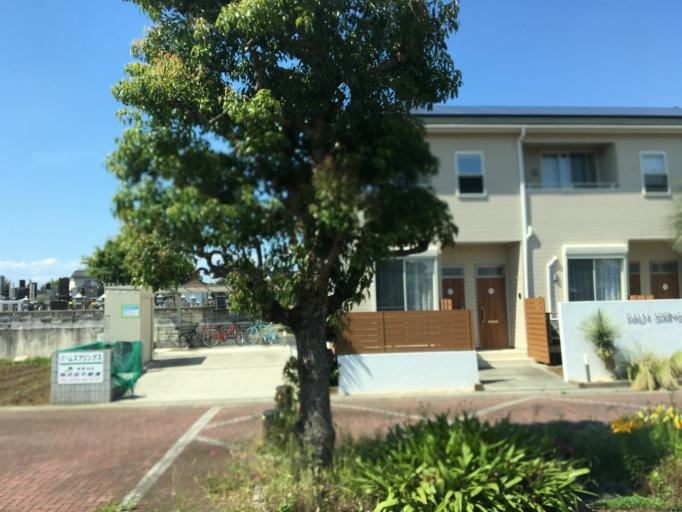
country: JP
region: Saitama
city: Sakado
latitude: 36.0028
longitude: 139.3904
